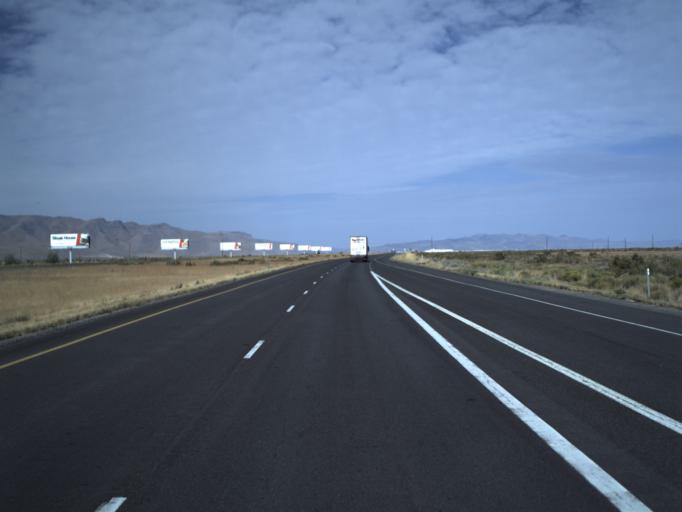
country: US
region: Utah
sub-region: Tooele County
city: Grantsville
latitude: 40.6867
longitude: -112.4504
